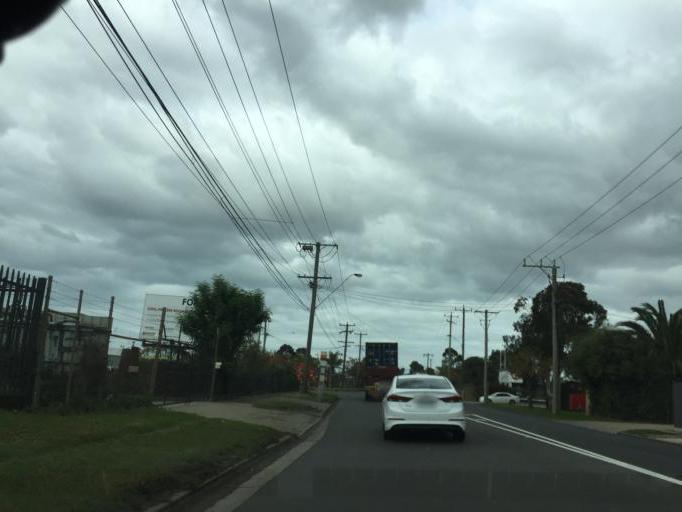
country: AU
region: Victoria
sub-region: Brimbank
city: Brooklyn
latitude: -37.8138
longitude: 144.8471
